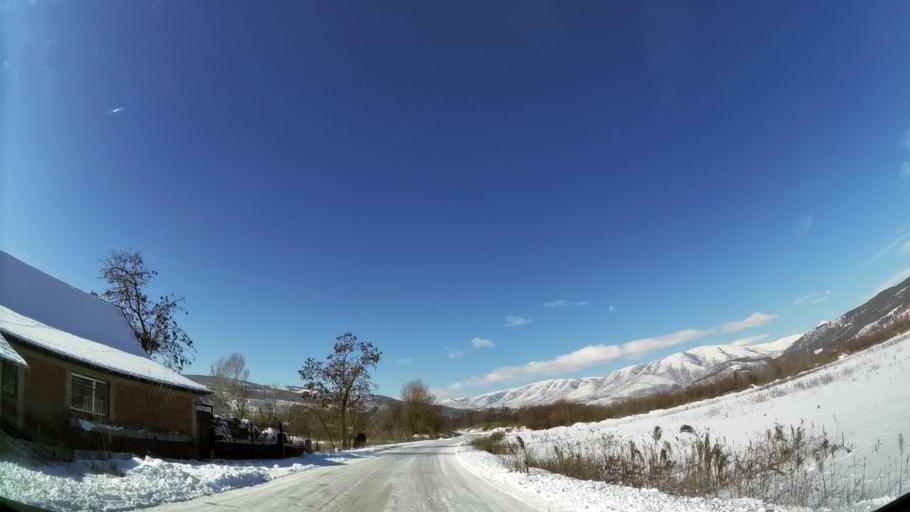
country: MK
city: Ljubin
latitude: 42.0047
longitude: 21.3067
